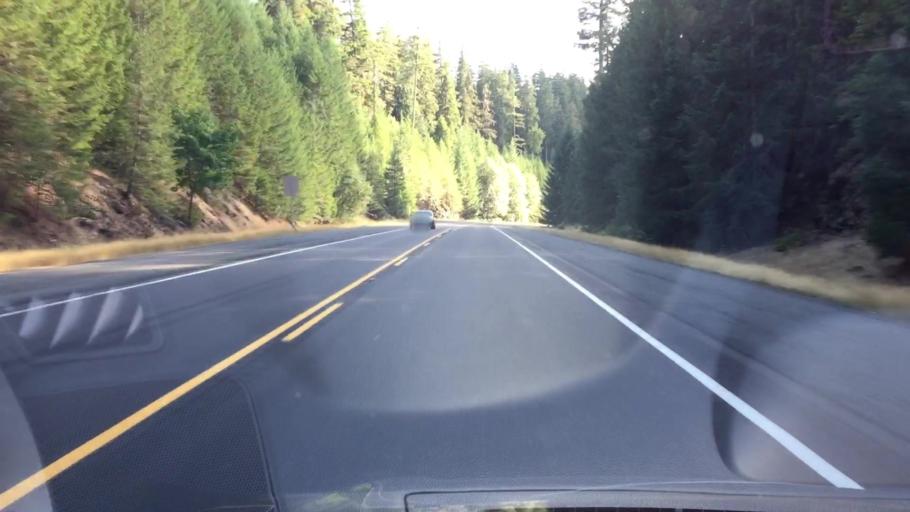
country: US
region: Washington
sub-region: Pierce County
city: Buckley
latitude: 46.6770
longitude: -121.5764
